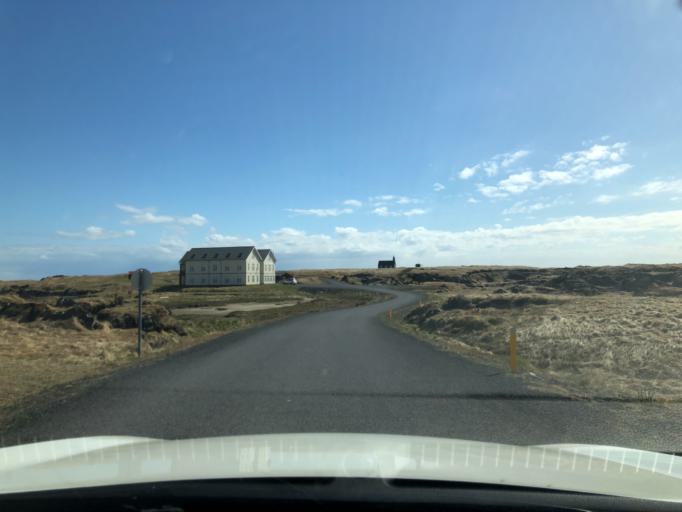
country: IS
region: West
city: Olafsvik
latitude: 64.8244
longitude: -23.3864
